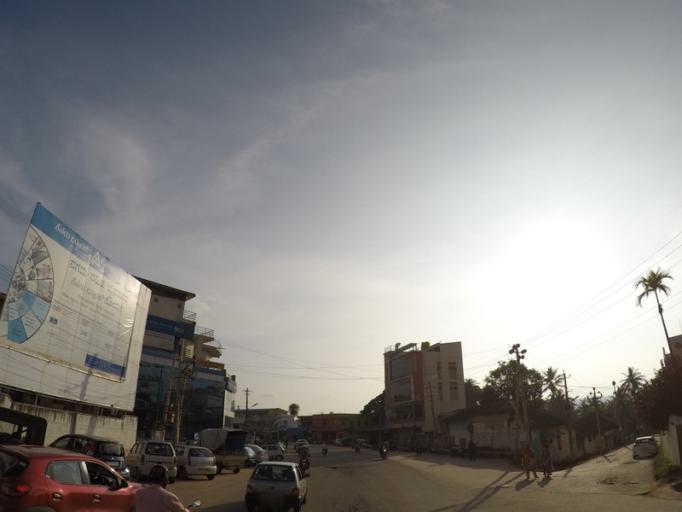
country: IN
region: Karnataka
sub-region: Chikmagalur
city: Chikmagalur
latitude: 13.3161
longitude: 75.7719
